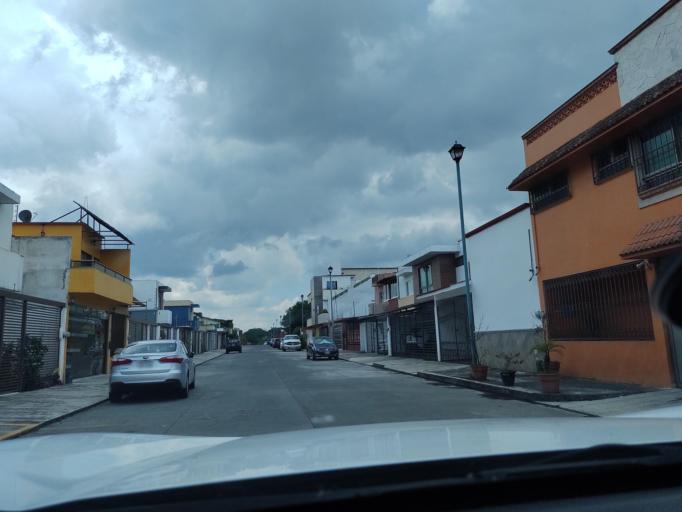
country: MX
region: Veracruz
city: Coatepec
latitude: 19.4479
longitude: -96.9512
